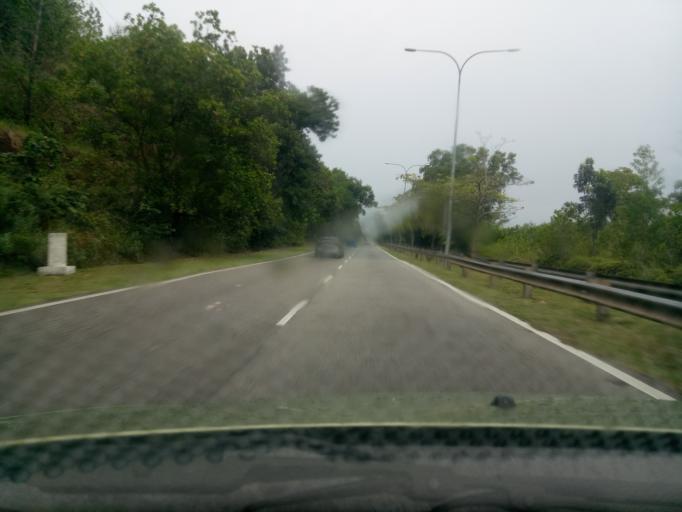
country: MY
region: Kedah
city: Sungai Petani
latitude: 5.6582
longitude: 100.5375
